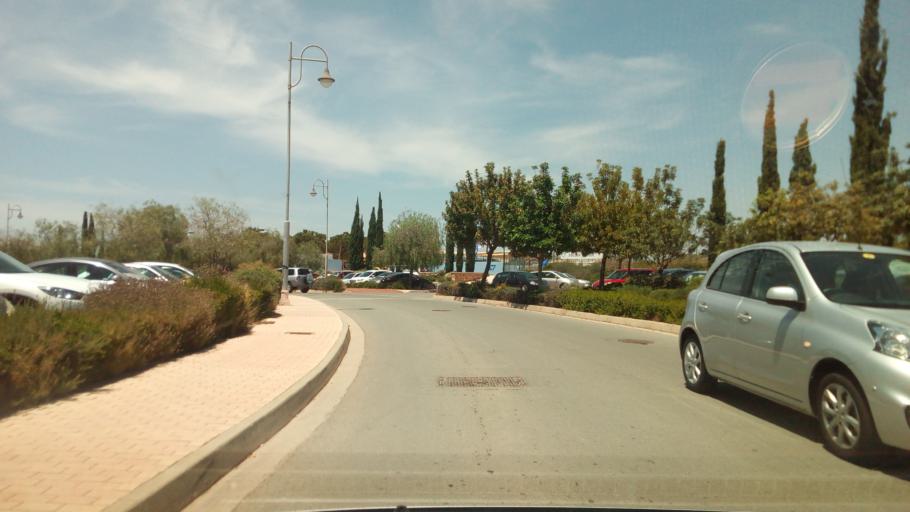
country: CY
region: Limassol
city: Pissouri
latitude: 34.6840
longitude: 32.6068
